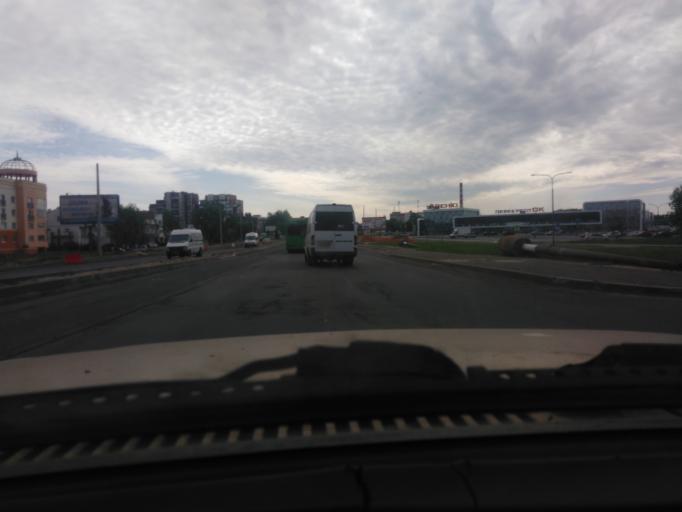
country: BY
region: Mogilev
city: Mahilyow
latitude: 53.9193
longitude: 30.2974
